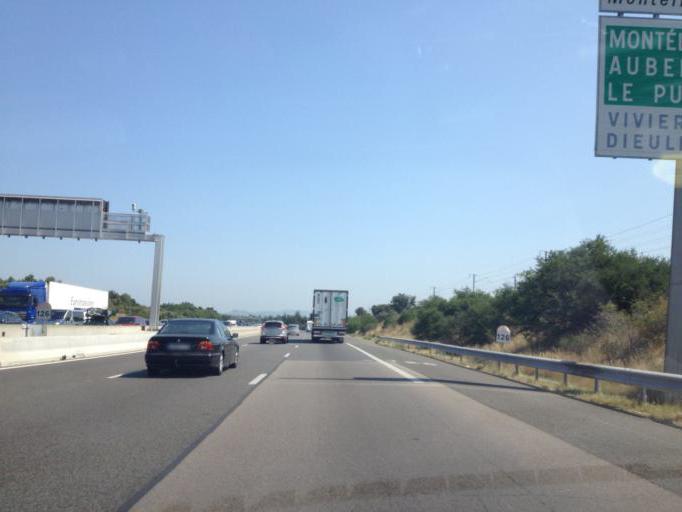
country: FR
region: Rhone-Alpes
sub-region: Departement de la Drome
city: Malataverne
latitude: 44.4683
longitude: 4.7643
